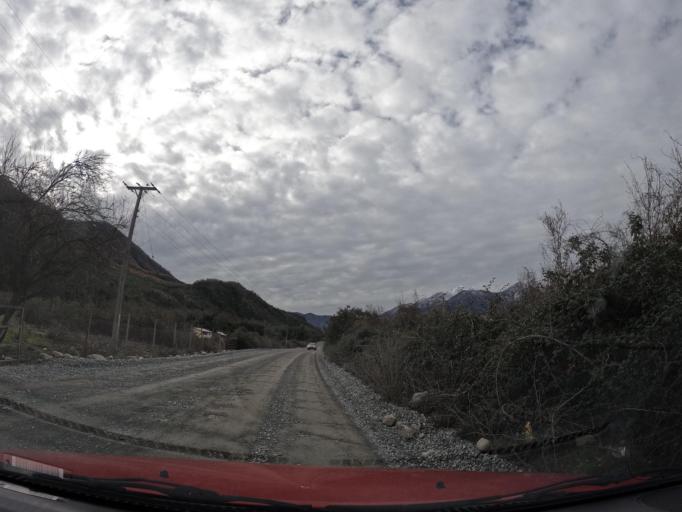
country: CL
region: Maule
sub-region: Provincia de Linares
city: Colbun
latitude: -35.8847
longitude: -71.2770
